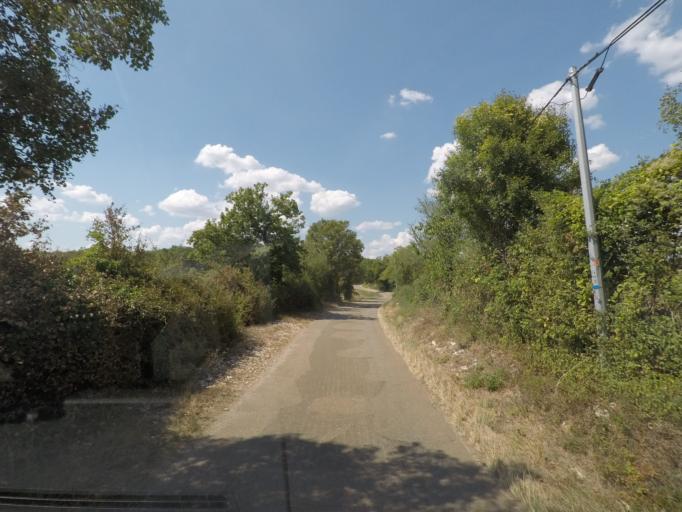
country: FR
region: Midi-Pyrenees
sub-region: Departement du Lot
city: Cahors
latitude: 44.5243
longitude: 1.6224
